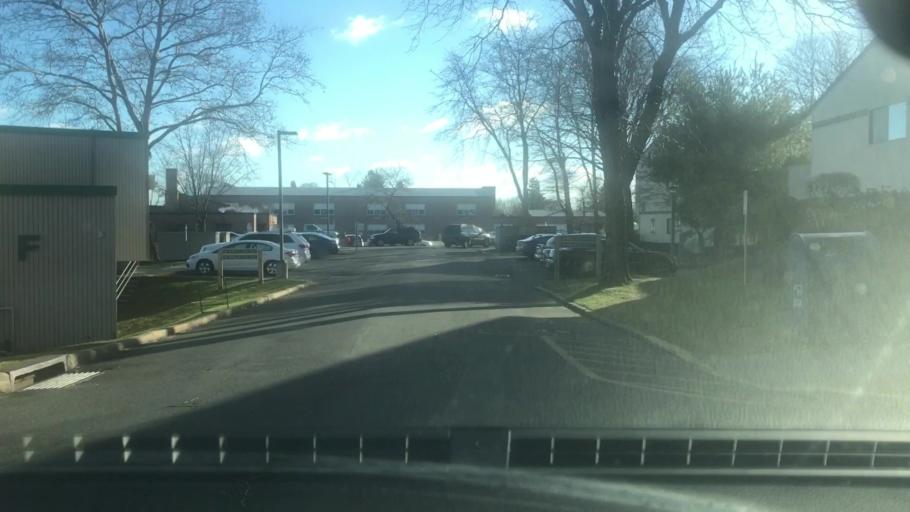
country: US
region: New York
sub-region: Rockland County
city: West Haverstraw
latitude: 41.2138
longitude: -73.9845
